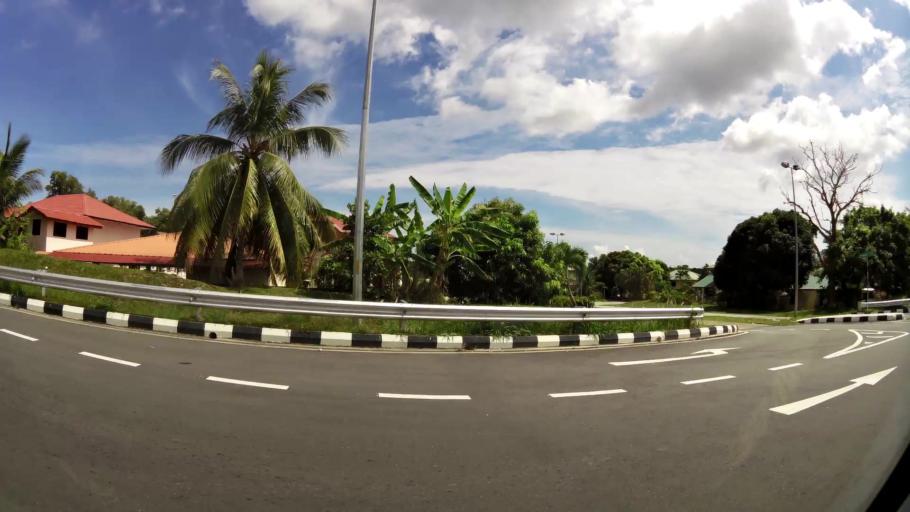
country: BN
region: Brunei and Muara
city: Bandar Seri Begawan
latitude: 4.9332
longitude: 114.8938
